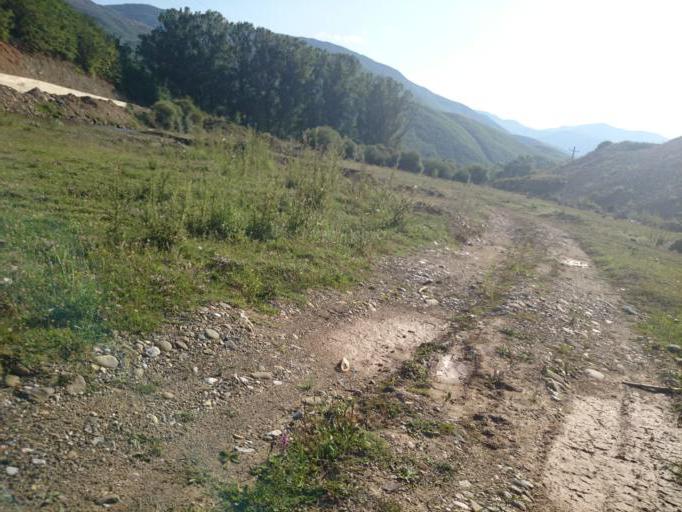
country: AL
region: Diber
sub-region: Rrethi i Bulqizes
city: Zerqan
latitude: 41.5138
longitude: 20.3868
